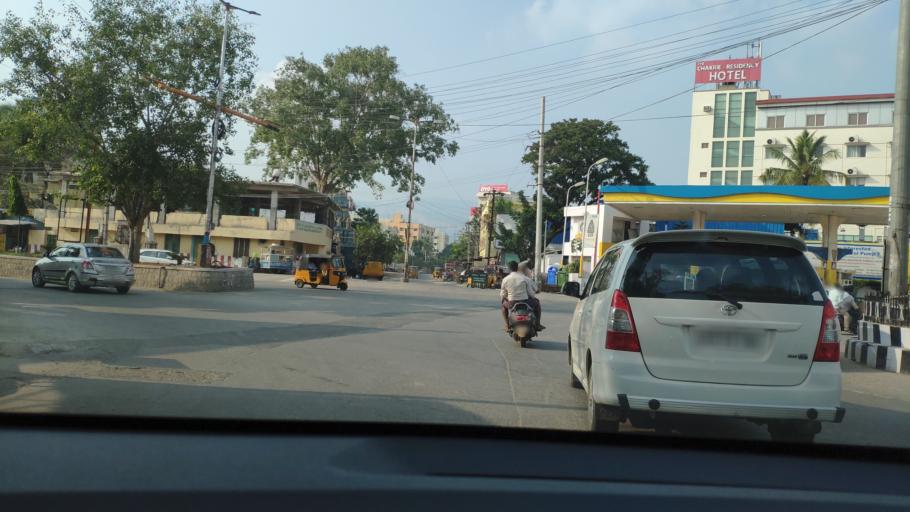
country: IN
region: Andhra Pradesh
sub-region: Chittoor
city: Tirupati
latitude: 13.6224
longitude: 79.4302
